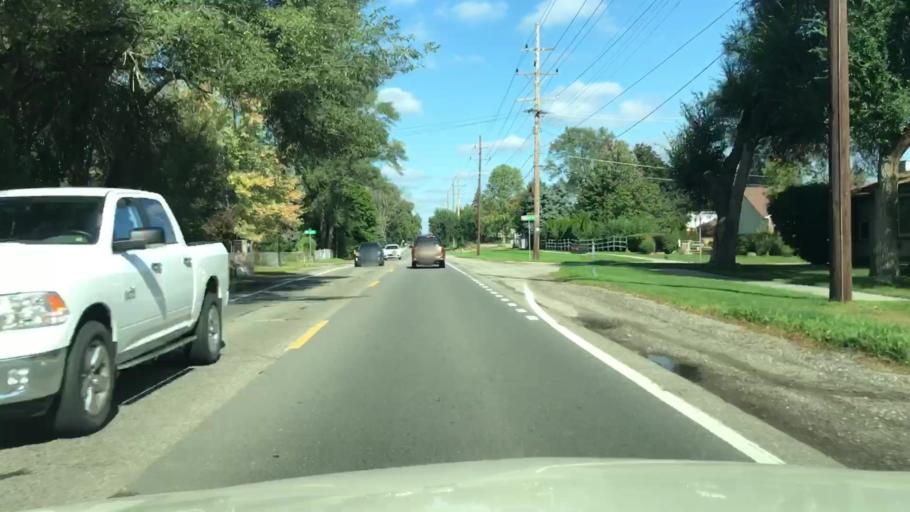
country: US
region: Michigan
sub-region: Oakland County
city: Rochester
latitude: 42.6432
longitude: -83.0923
